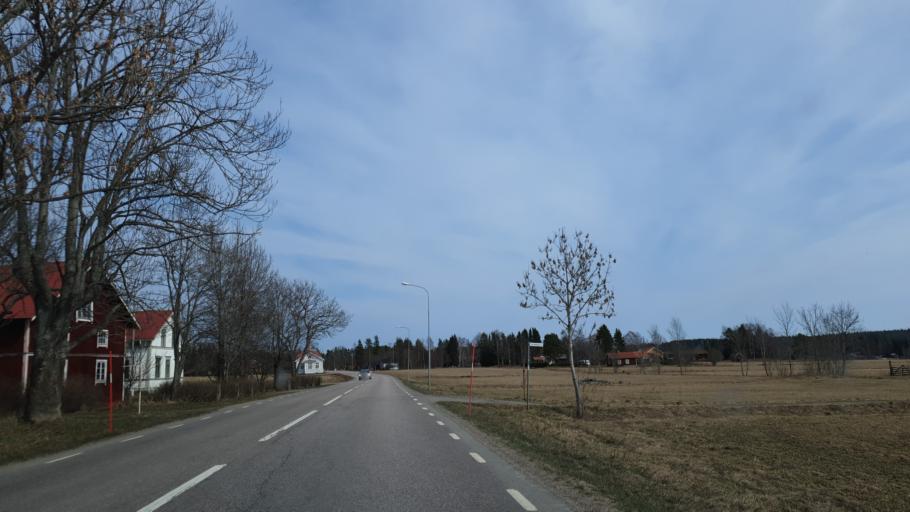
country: SE
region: Gaevleborg
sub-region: Gavle Kommun
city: Norrsundet
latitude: 61.0014
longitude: 17.1186
